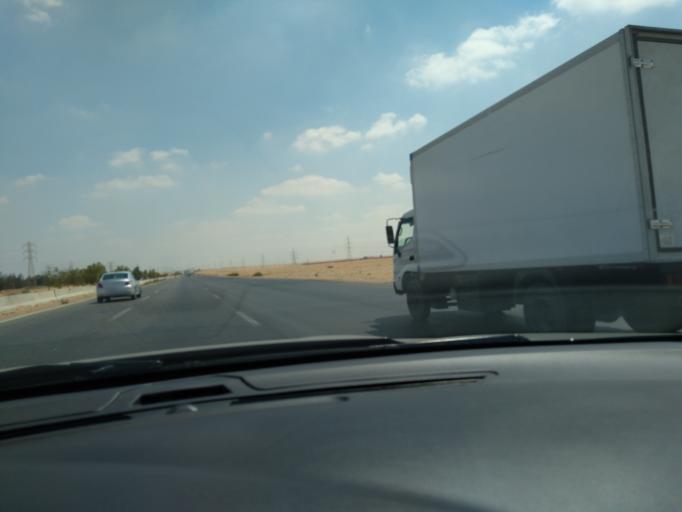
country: EG
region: Al Isma'iliyah
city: At Tall al Kabir
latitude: 30.3576
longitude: 31.8991
